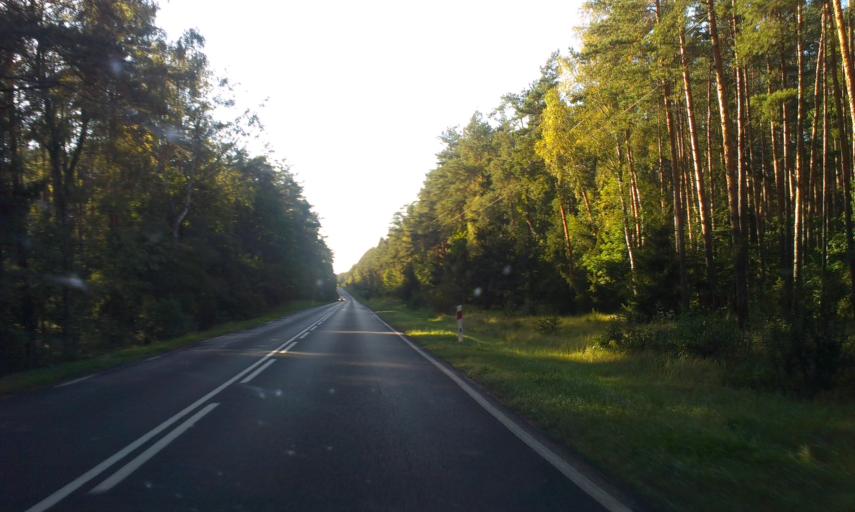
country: PL
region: Kujawsko-Pomorskie
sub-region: Powiat tucholski
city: Tuchola
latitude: 53.5518
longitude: 17.9215
